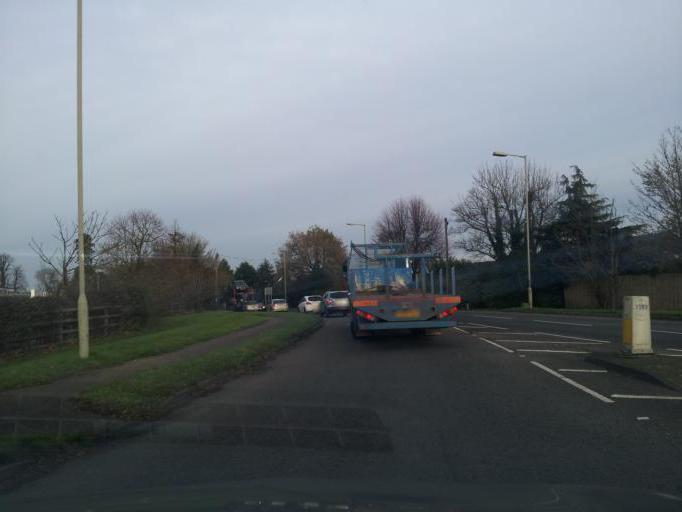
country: GB
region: England
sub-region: Buckinghamshire
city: Stewkley
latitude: 51.8912
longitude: -0.7228
